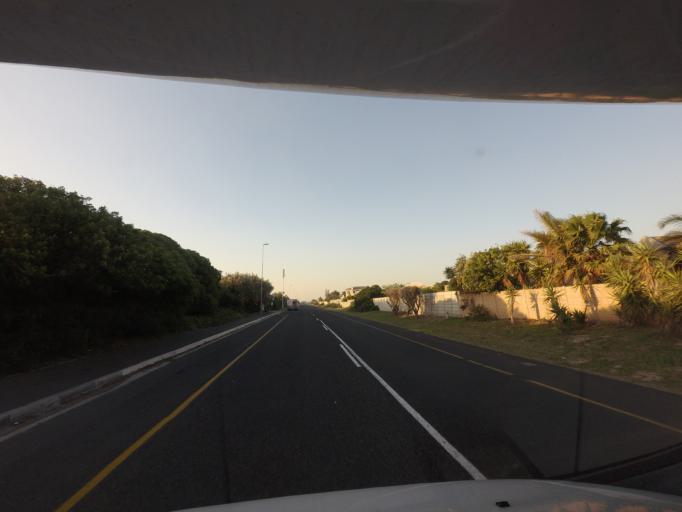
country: ZA
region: Western Cape
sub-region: City of Cape Town
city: Sunset Beach
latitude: -33.7235
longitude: 18.4474
